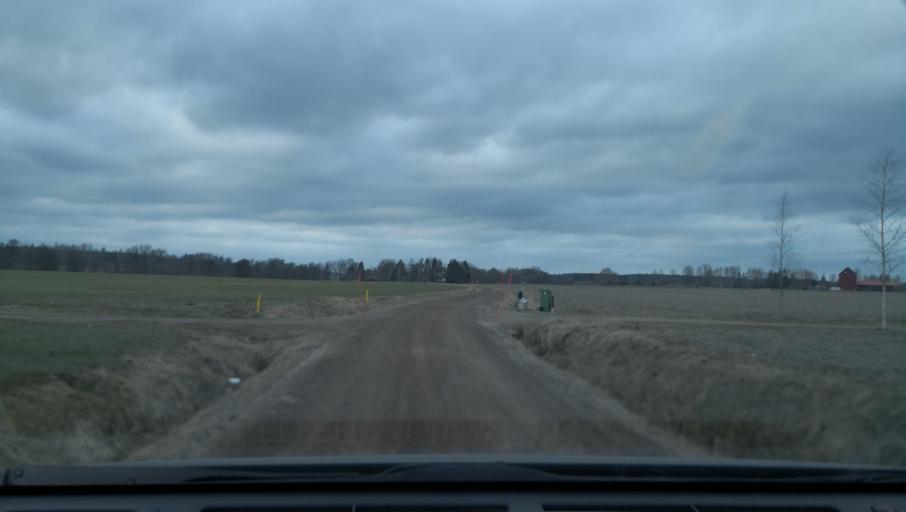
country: SE
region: Vaestmanland
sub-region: Kopings Kommun
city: Kolsva
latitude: 59.5357
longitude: 15.8947
